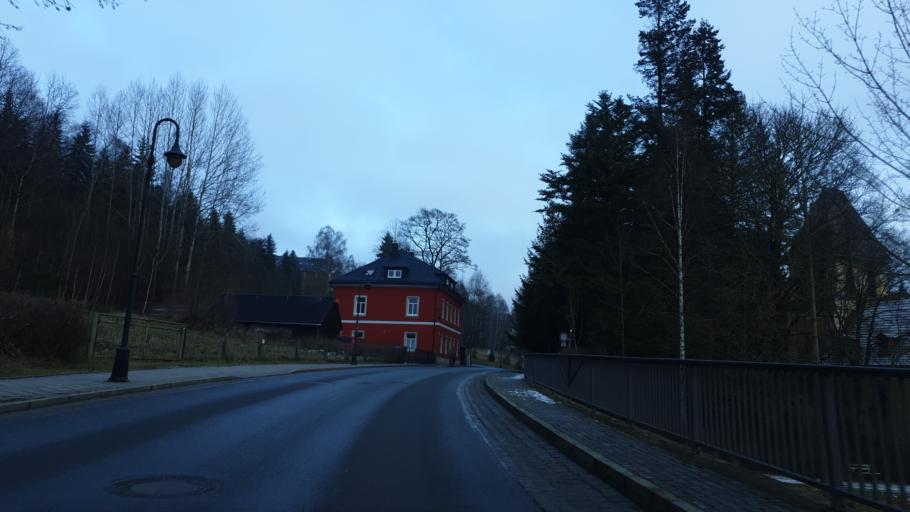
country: DE
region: Saxony
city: Bad Elster
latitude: 50.2779
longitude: 12.2410
